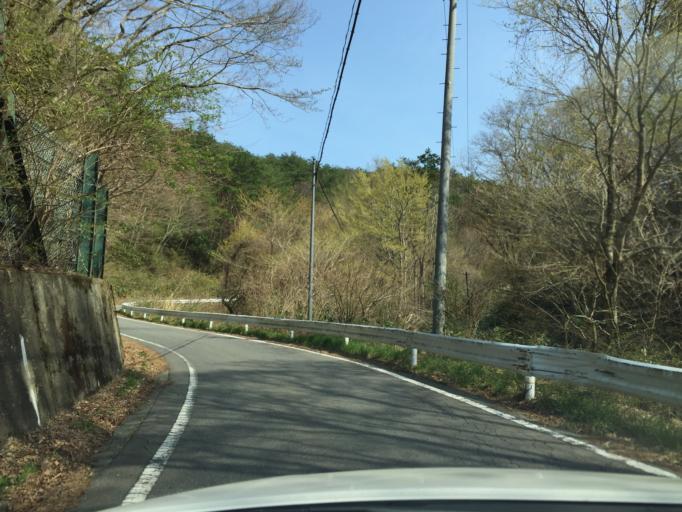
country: JP
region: Fukushima
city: Iwaki
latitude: 37.2230
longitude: 140.8478
